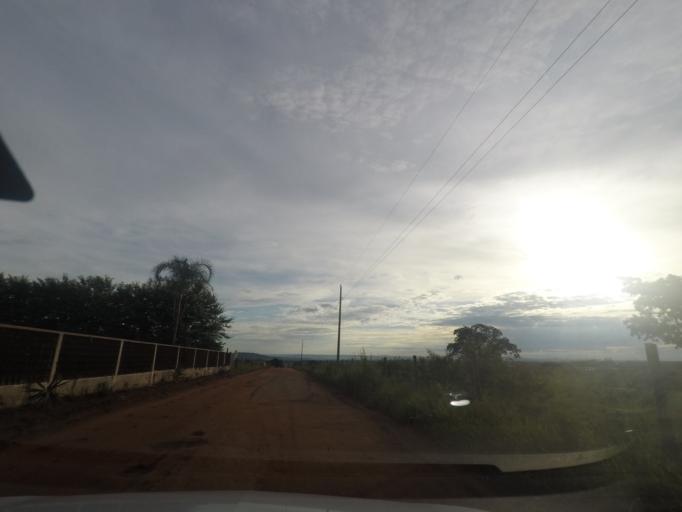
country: BR
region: Goias
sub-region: Trindade
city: Trindade
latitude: -16.7325
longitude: -49.4142
